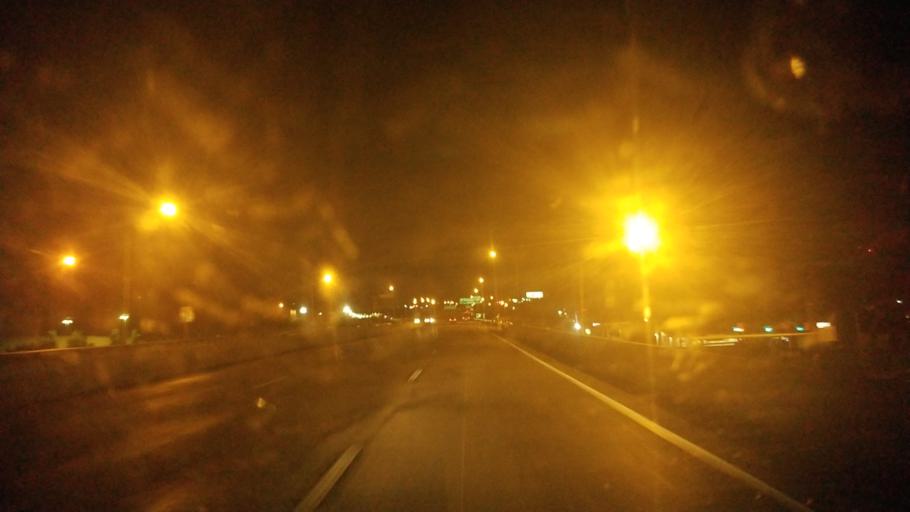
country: US
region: Missouri
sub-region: Saint Louis County
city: Black Jack
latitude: 38.7711
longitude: -90.2670
